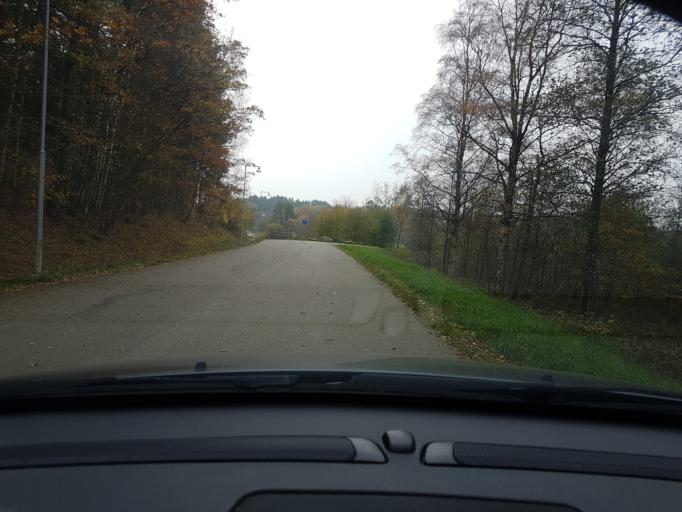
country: SE
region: Vaestra Goetaland
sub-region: Ale Kommun
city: Alafors
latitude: 57.9438
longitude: 12.0992
